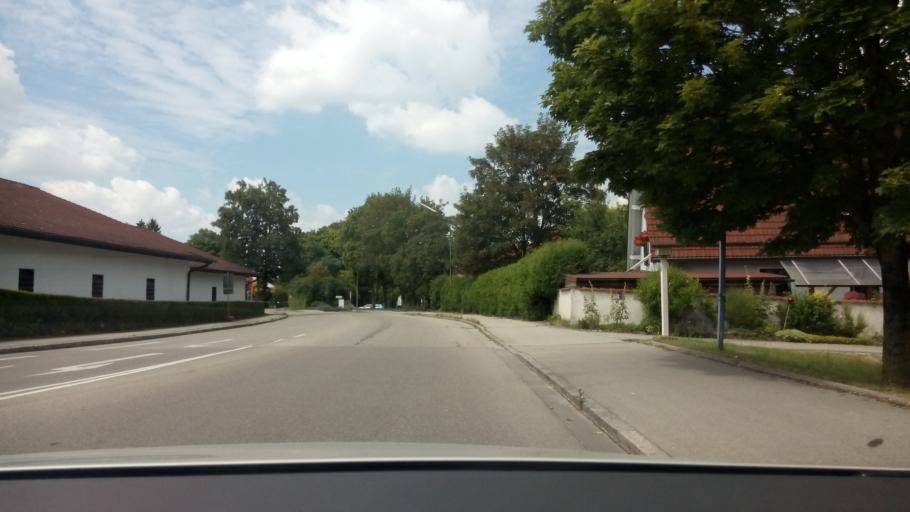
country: DE
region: Bavaria
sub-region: Upper Bavaria
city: Neufahrn bei Freising
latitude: 48.3158
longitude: 11.6895
